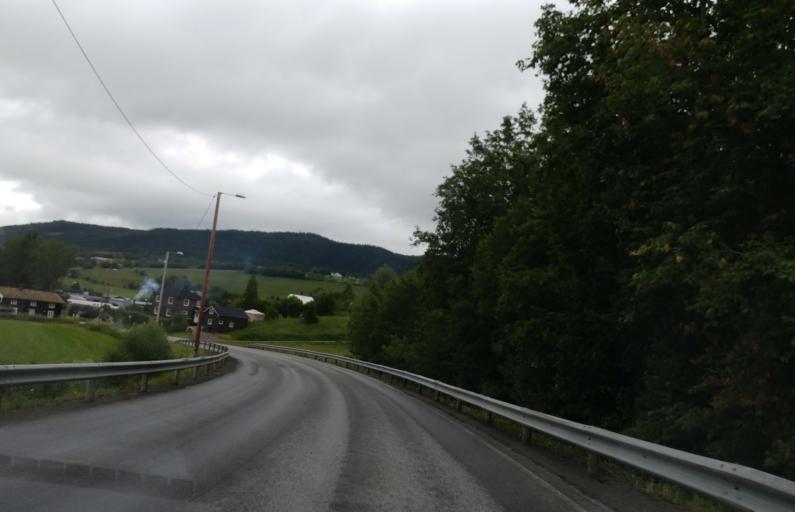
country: NO
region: Sor-Trondelag
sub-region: Selbu
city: Mebonden
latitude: 63.2402
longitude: 11.0696
